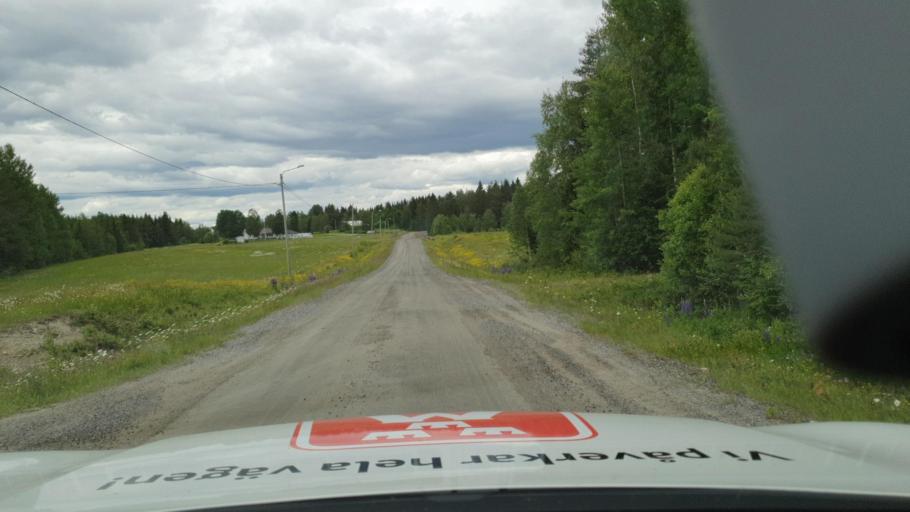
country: SE
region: Vaesterbotten
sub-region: Bjurholms Kommun
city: Bjurholm
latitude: 63.7595
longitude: 19.2647
